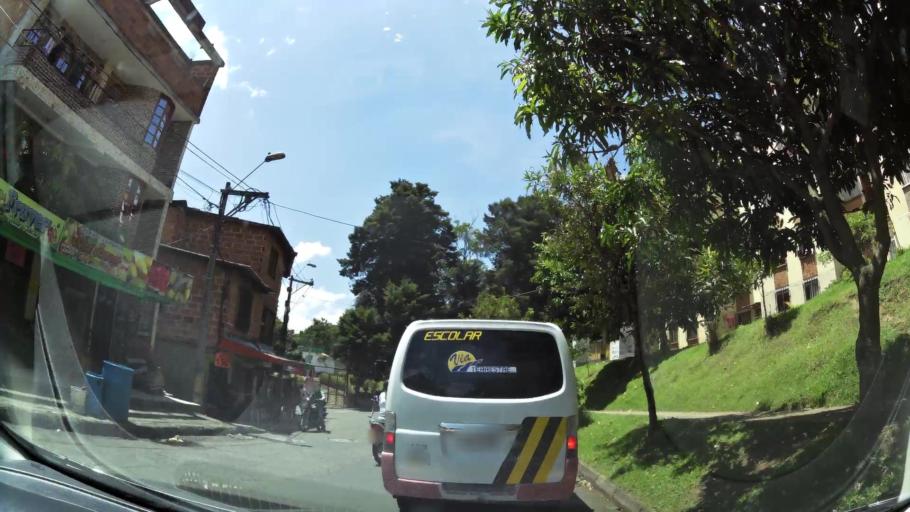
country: CO
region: Antioquia
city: La Estrella
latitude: 6.1831
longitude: -75.6483
